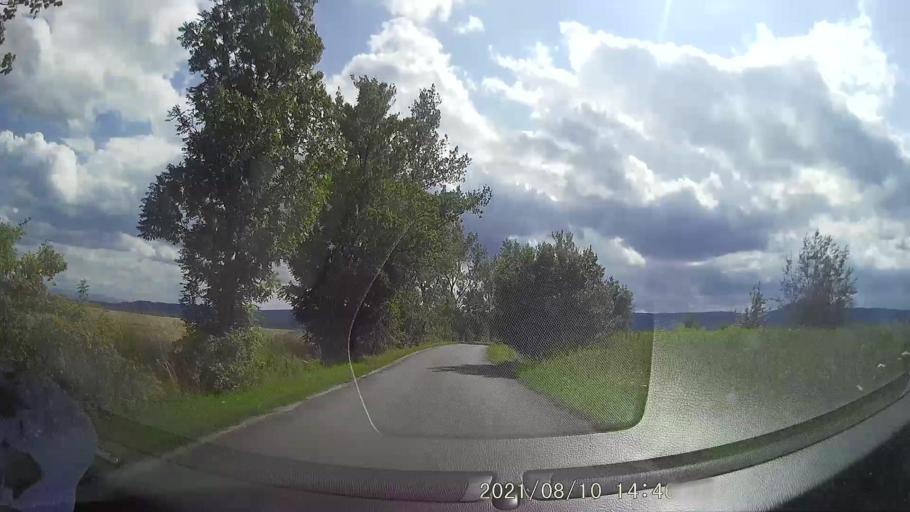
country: PL
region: Lower Silesian Voivodeship
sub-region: Powiat klodzki
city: Radkow
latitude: 50.5271
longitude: 16.4125
